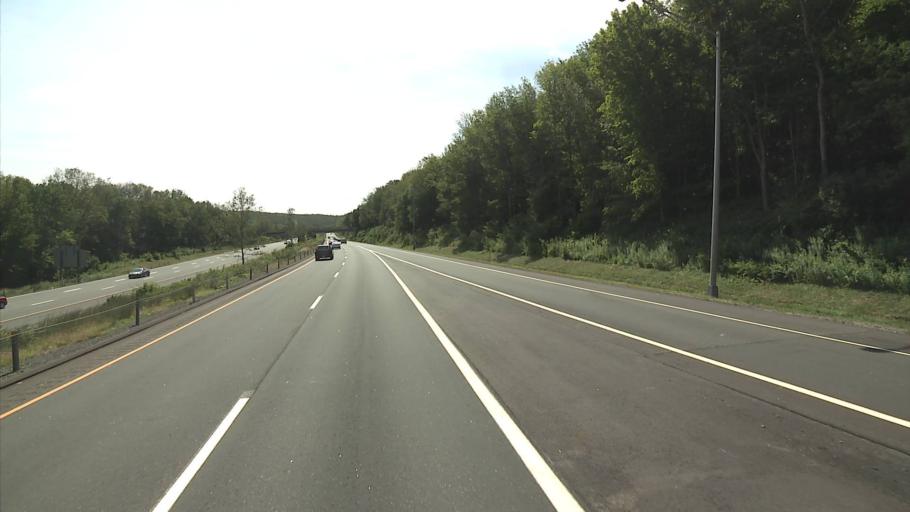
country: US
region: Connecticut
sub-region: Hartford County
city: Terramuggus
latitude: 41.6321
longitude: -72.4554
